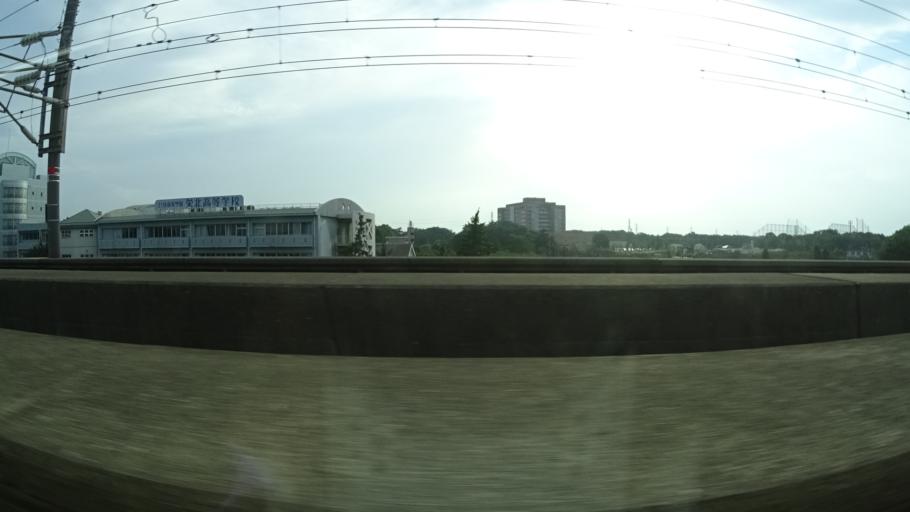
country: JP
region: Saitama
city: Ageoshimo
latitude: 35.9853
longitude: 139.6242
